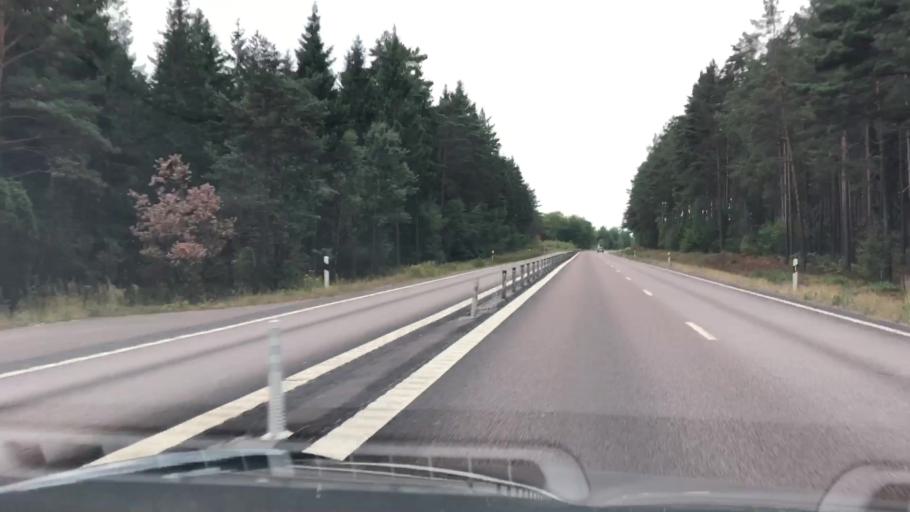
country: SE
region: Blekinge
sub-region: Karlskrona Kommun
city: Jaemjoe
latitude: 56.2462
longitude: 15.9348
